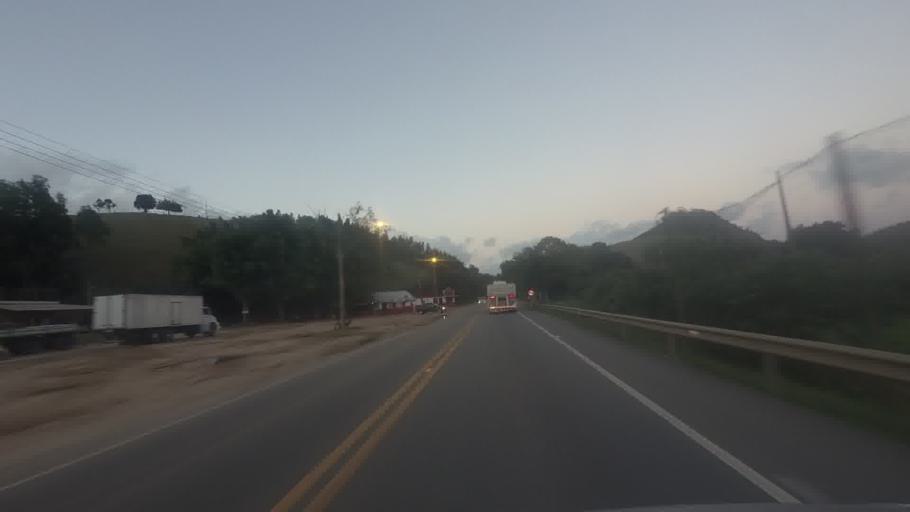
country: BR
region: Espirito Santo
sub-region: Rio Novo Do Sul
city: Rio Novo do Sul
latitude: -20.8379
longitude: -40.8693
